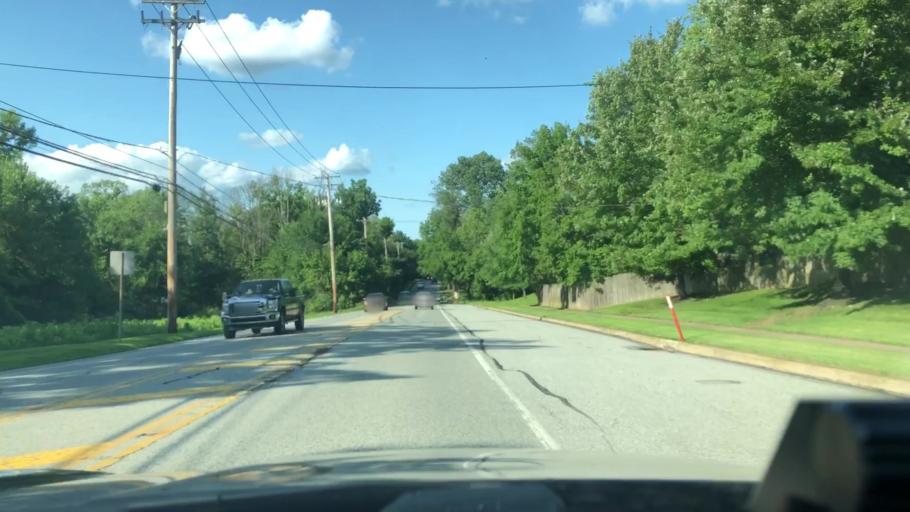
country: US
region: Pennsylvania
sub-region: Montgomery County
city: Montgomeryville
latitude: 40.2586
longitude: -75.2354
